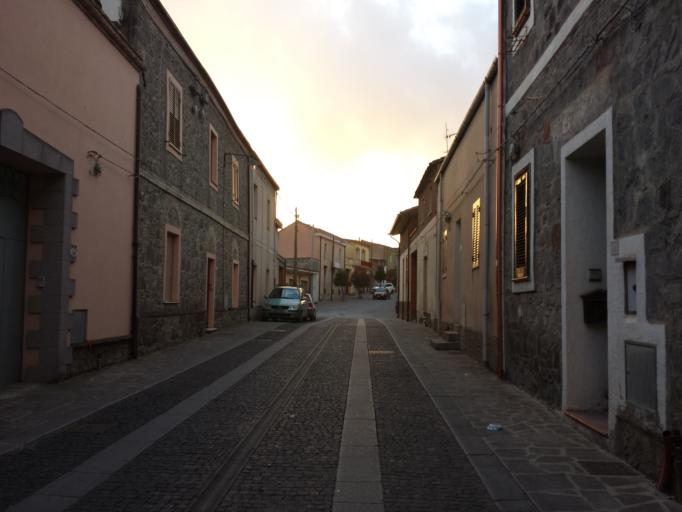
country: IT
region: Sardinia
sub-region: Provincia di Medio Campidano
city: Serrenti
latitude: 39.4951
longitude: 8.9768
